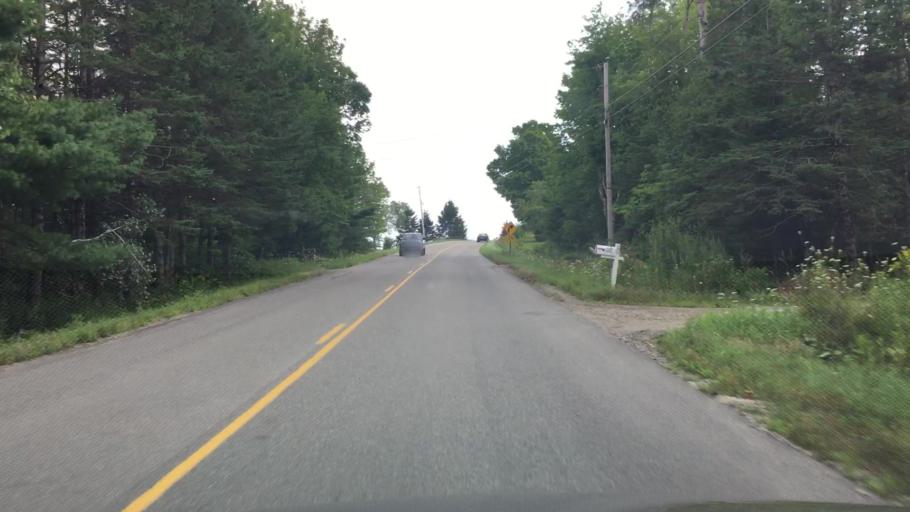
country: US
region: Maine
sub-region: Waldo County
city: Winterport
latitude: 44.6822
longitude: -68.8691
